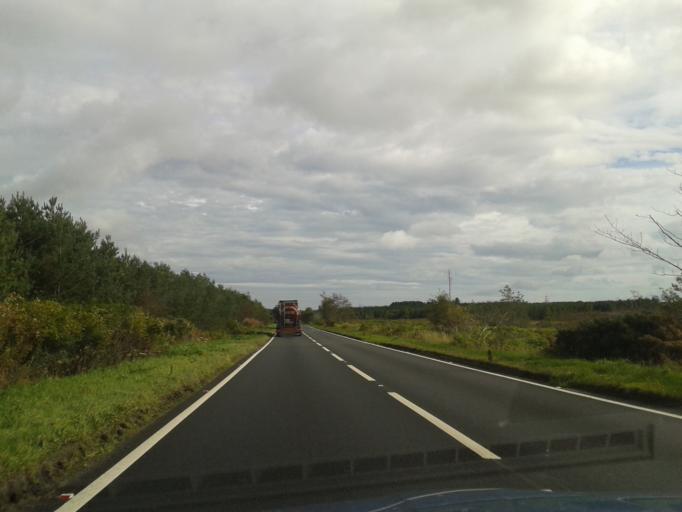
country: GB
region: Scotland
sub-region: Moray
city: Burghead
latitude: 57.6353
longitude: -3.4835
